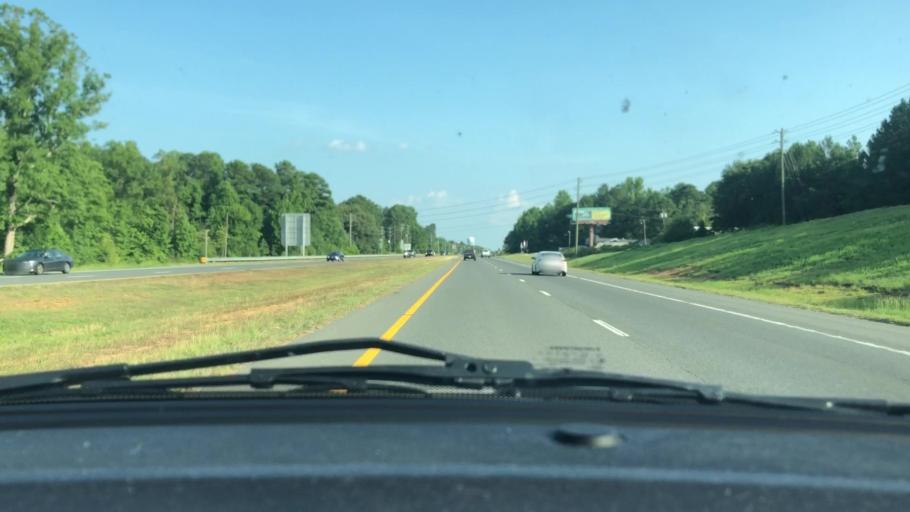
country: US
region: North Carolina
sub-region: Lee County
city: Broadway
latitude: 35.4282
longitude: -79.1221
